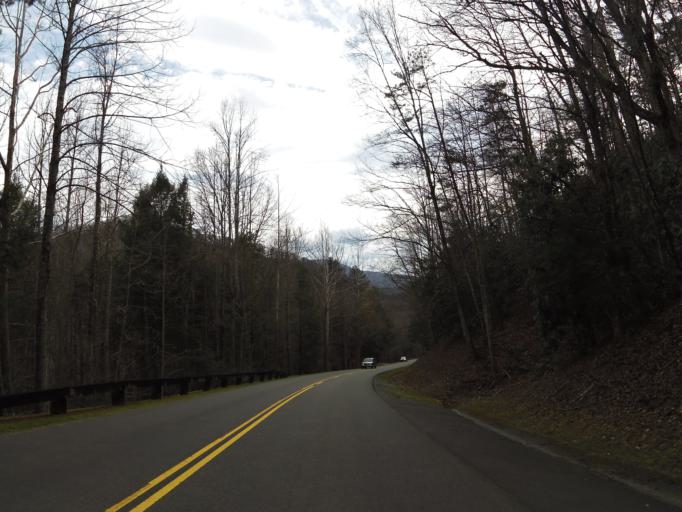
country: US
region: Tennessee
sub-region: Sevier County
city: Gatlinburg
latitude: 35.7001
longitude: -83.5292
